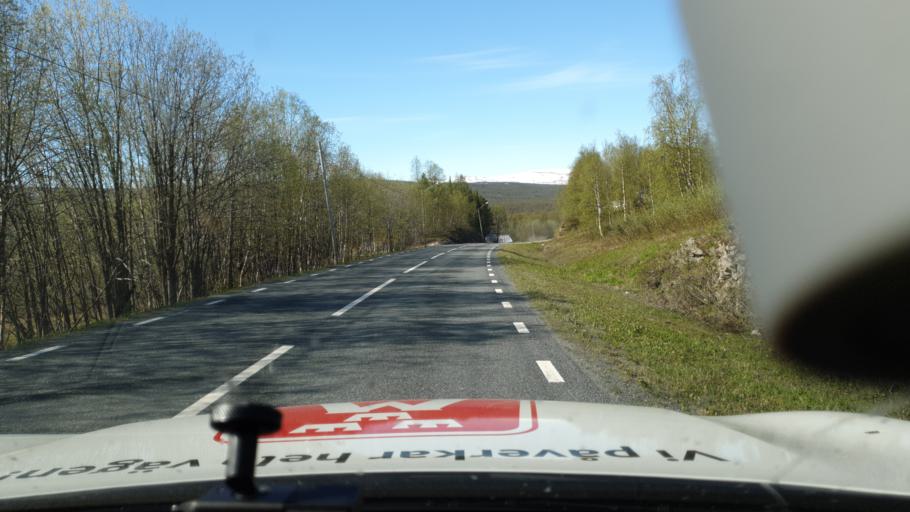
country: NO
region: Nordland
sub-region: Rana
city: Mo i Rana
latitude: 65.7550
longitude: 15.1119
